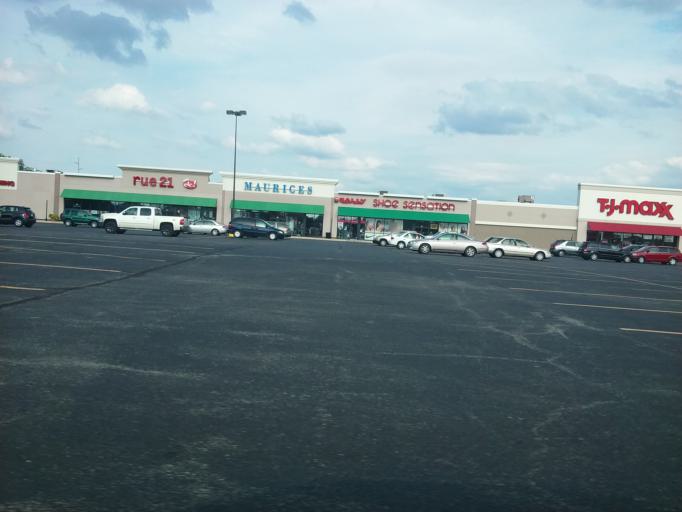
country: US
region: Ohio
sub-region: Wood County
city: Bowling Green
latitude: 41.3559
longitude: -83.6495
